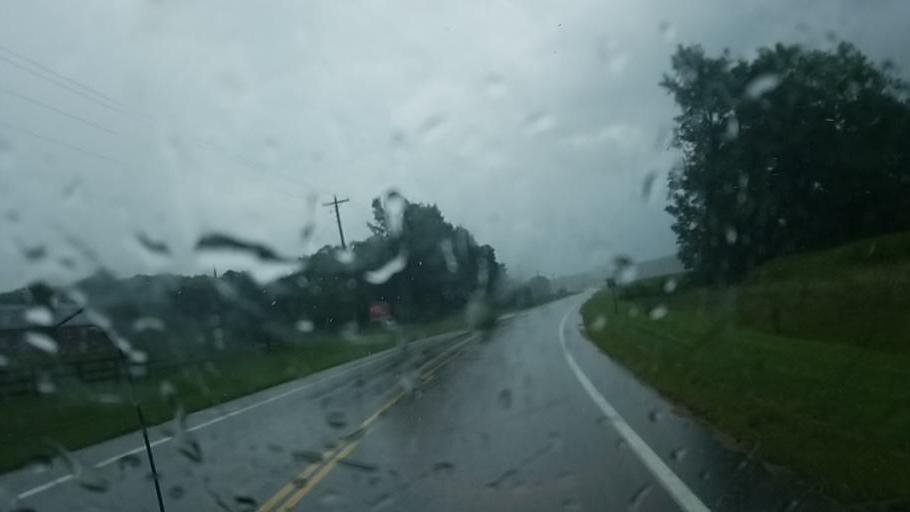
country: US
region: Ohio
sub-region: Logan County
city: Bellefontaine
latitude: 40.3278
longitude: -83.6605
